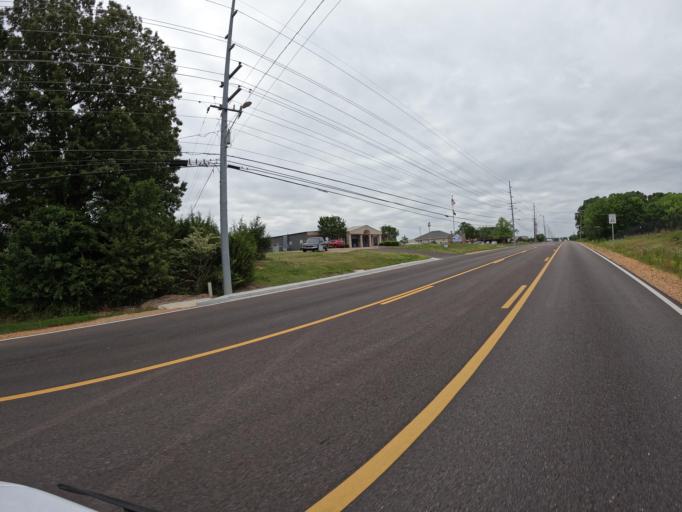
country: US
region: Mississippi
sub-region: Lee County
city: Tupelo
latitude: 34.2700
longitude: -88.7643
